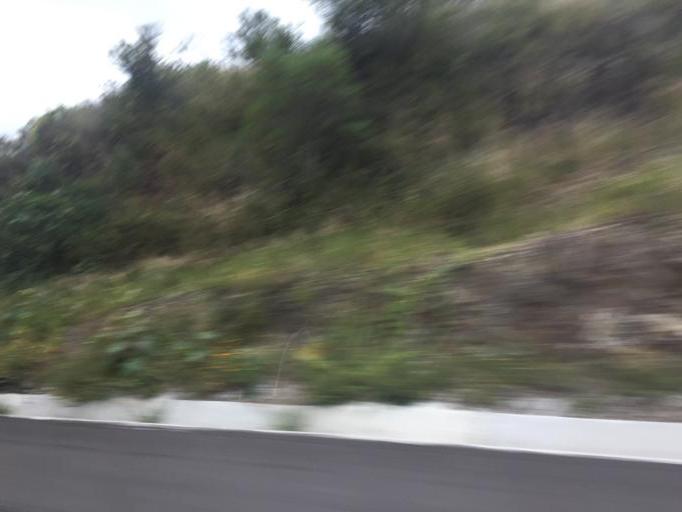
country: MX
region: Jalisco
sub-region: Poncitlan
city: Santa Cruz el Grande
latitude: 20.4428
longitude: -102.8285
